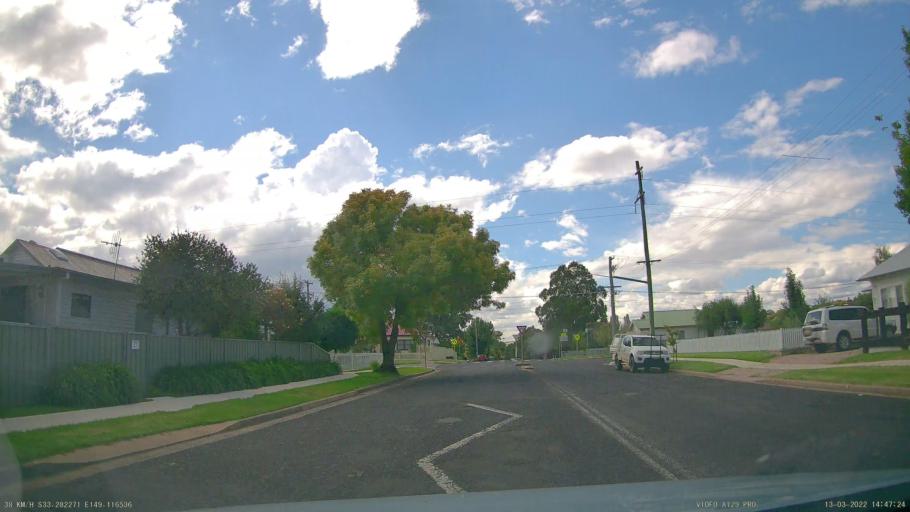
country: AU
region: New South Wales
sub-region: Orange Municipality
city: Orange
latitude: -33.2822
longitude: 149.1166
